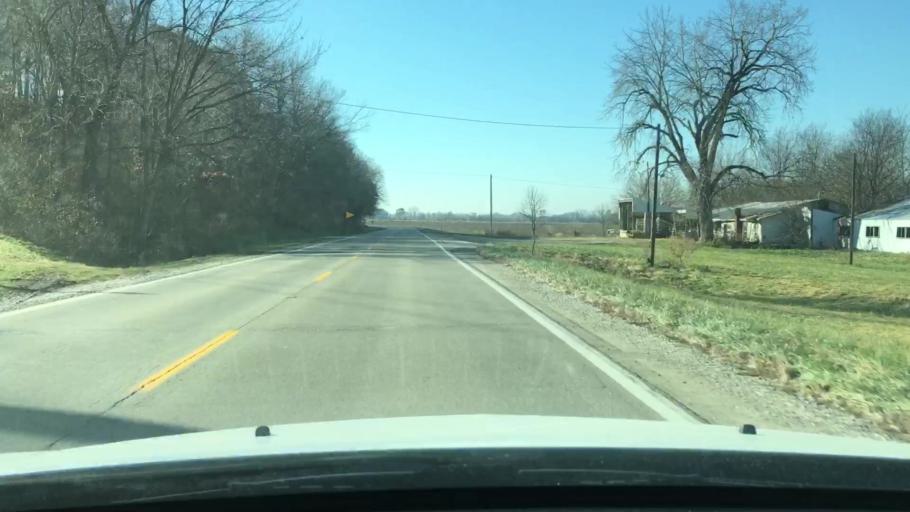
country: US
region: Illinois
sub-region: Morgan County
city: Meredosia
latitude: 39.7369
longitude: -90.5588
